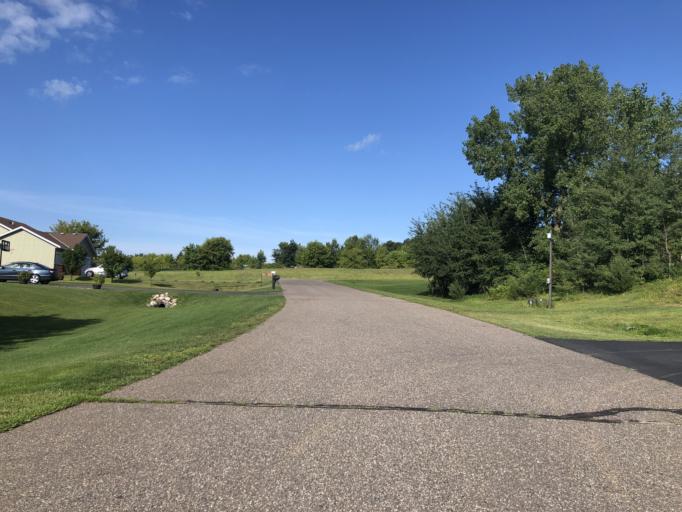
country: US
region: Minnesota
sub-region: Sherburne County
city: Becker
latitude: 45.4213
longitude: -93.8347
